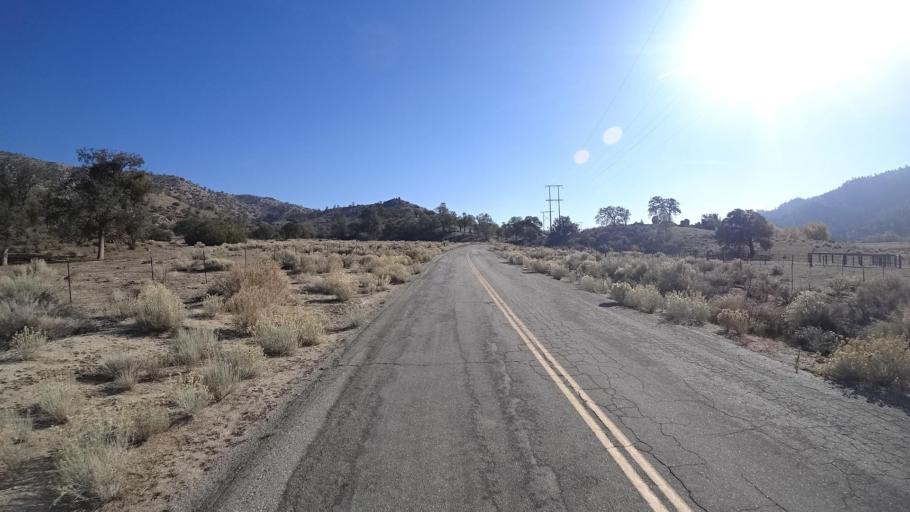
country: US
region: California
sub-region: Kern County
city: Bodfish
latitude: 35.3956
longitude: -118.4389
